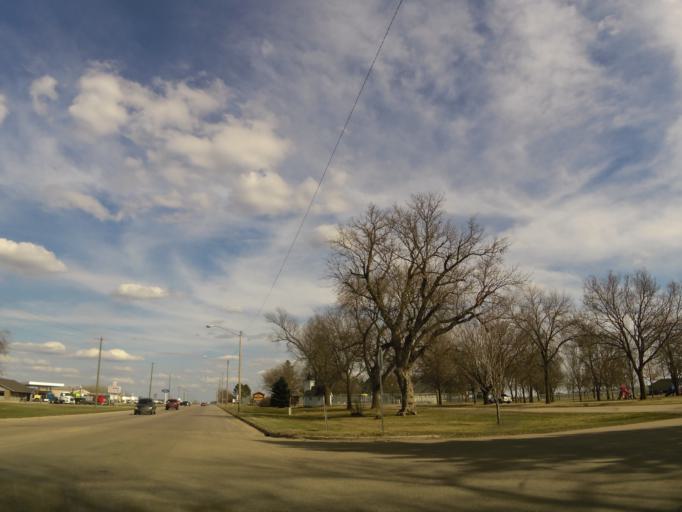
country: US
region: Minnesota
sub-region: Lac qui Parle County
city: Dawson
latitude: 44.9358
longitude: -96.0478
